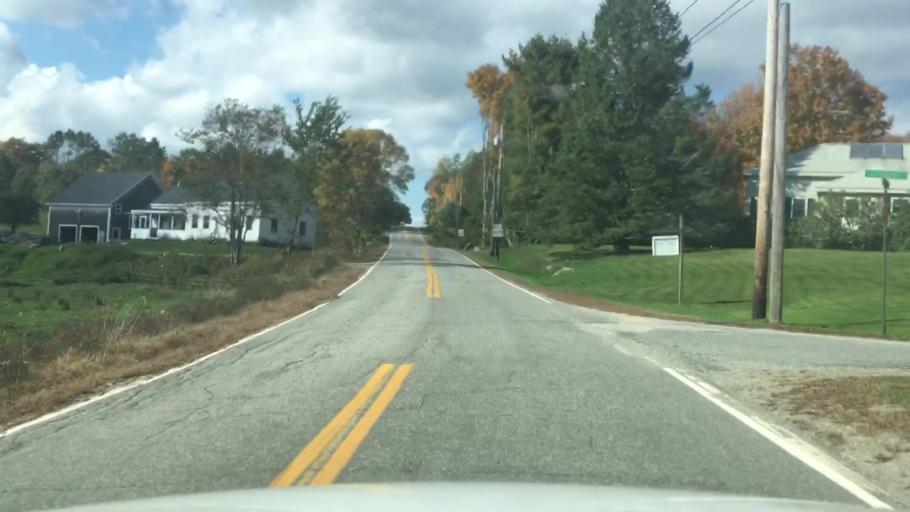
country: US
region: Maine
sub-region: Knox County
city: Washington
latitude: 44.2983
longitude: -69.3181
